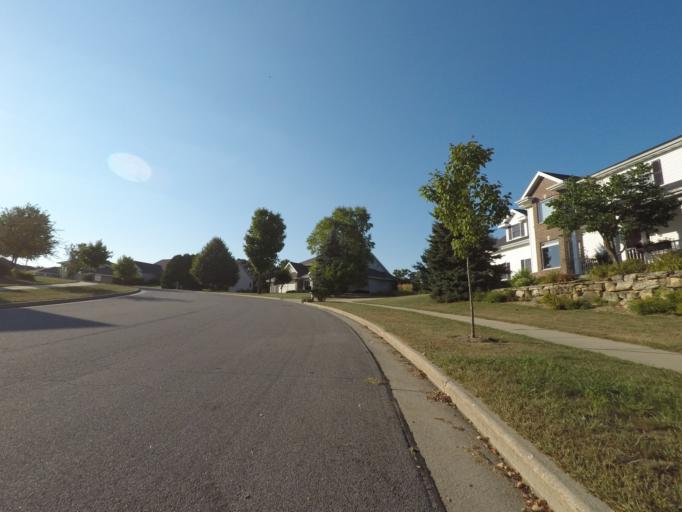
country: US
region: Wisconsin
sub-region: Dane County
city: Verona
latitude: 43.0064
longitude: -89.5346
